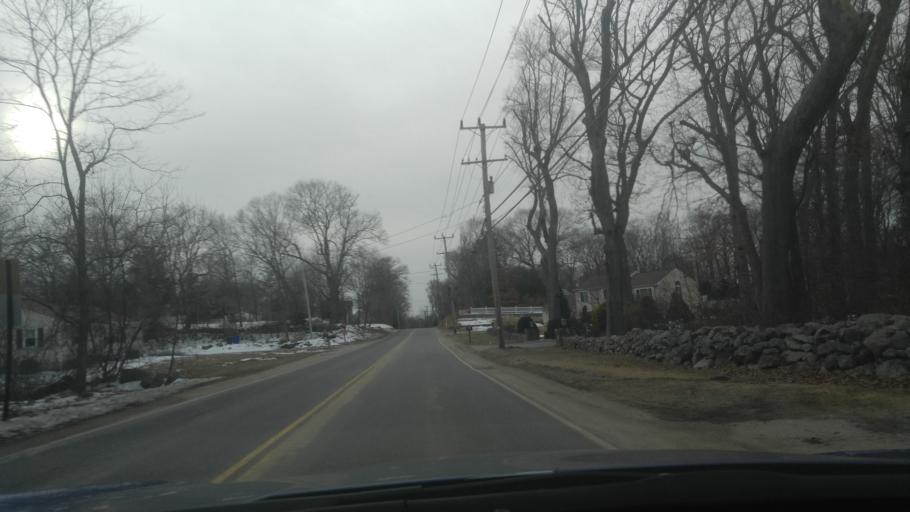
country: US
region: Rhode Island
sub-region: Kent County
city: West Warwick
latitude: 41.6734
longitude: -71.5139
